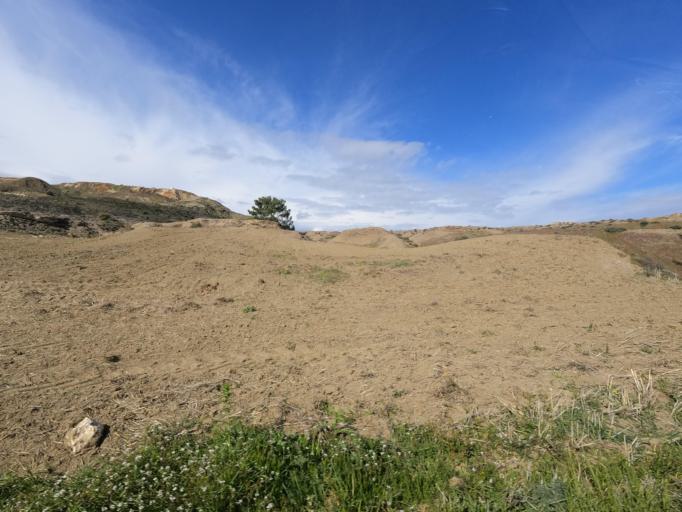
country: CY
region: Lefkosia
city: Lefka
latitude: 35.1016
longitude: 32.9016
